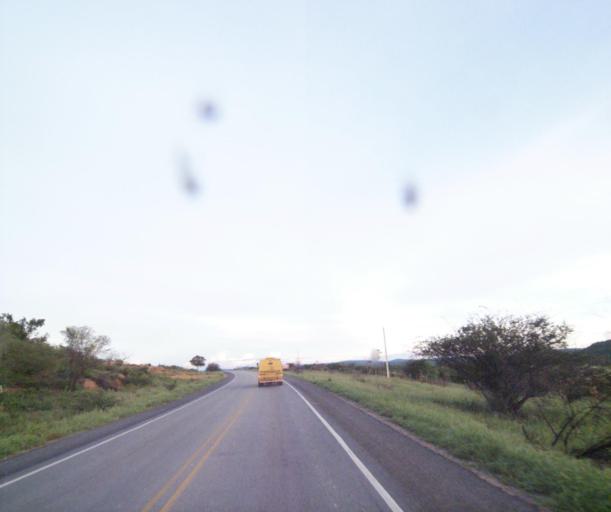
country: BR
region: Bahia
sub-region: Brumado
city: Brumado
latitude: -14.2533
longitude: -41.7411
